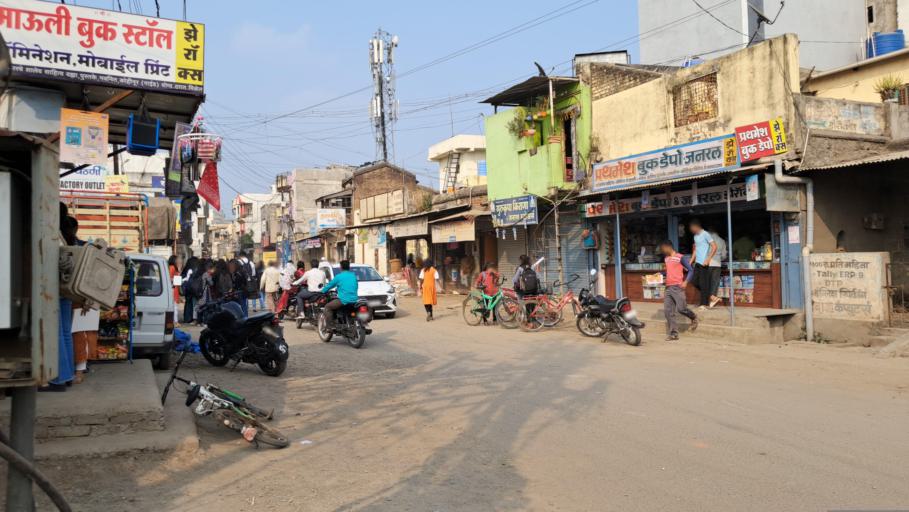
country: IN
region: Maharashtra
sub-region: Nashik Division
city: Yeola
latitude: 20.0385
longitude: 74.4897
